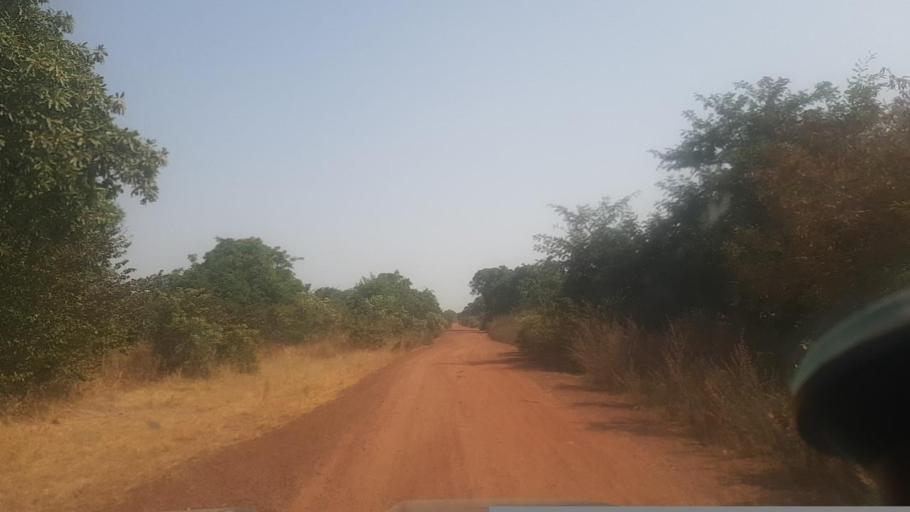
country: ML
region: Segou
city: Bla
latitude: 12.9235
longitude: -6.2656
